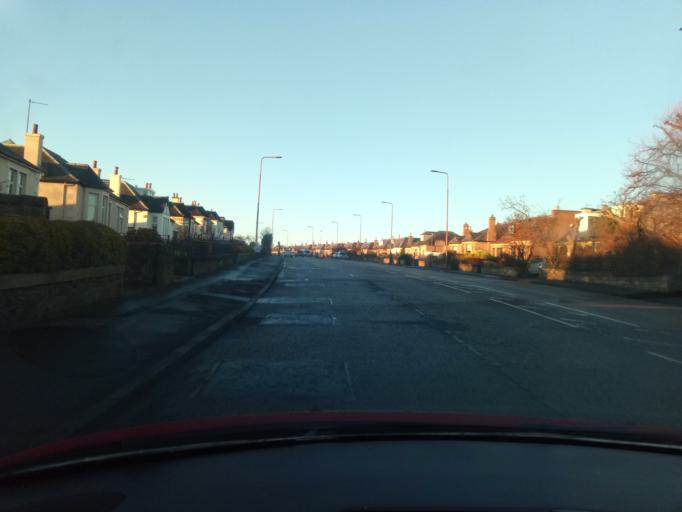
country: GB
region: Scotland
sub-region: East Lothian
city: Musselburgh
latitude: 55.9467
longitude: -3.0828
